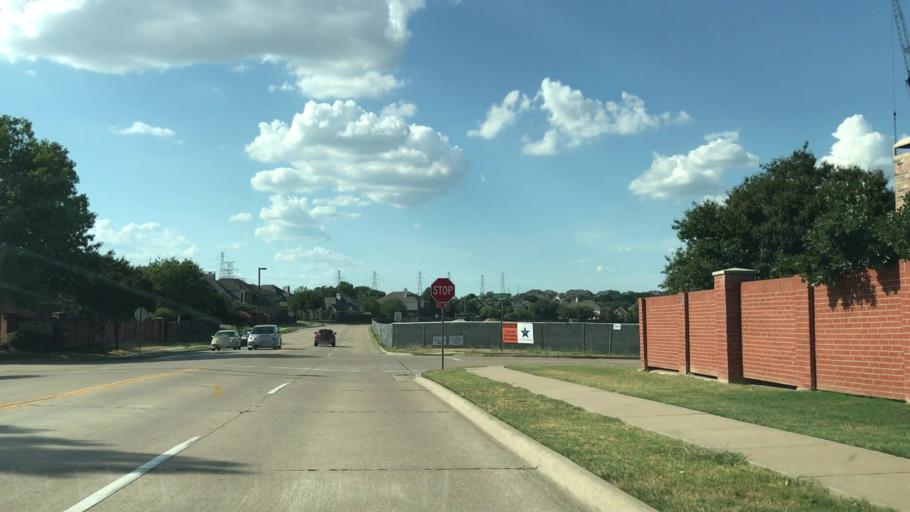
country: US
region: Texas
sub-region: Dallas County
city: Coppell
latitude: 32.9346
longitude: -96.9651
